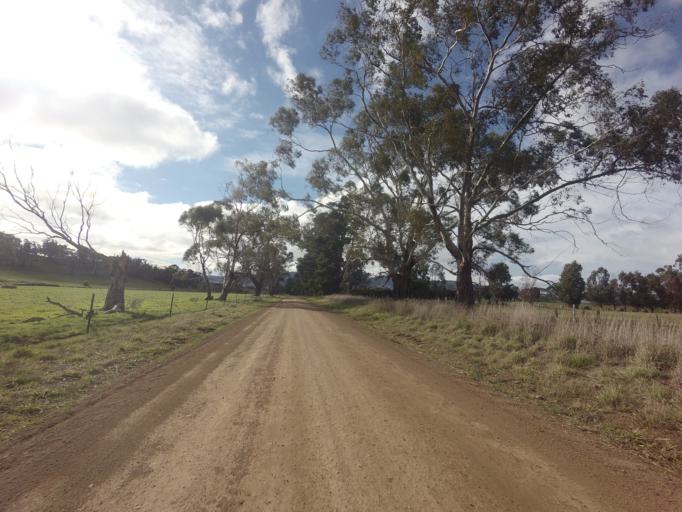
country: AU
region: Tasmania
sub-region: Derwent Valley
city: New Norfolk
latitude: -42.7138
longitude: 146.8873
